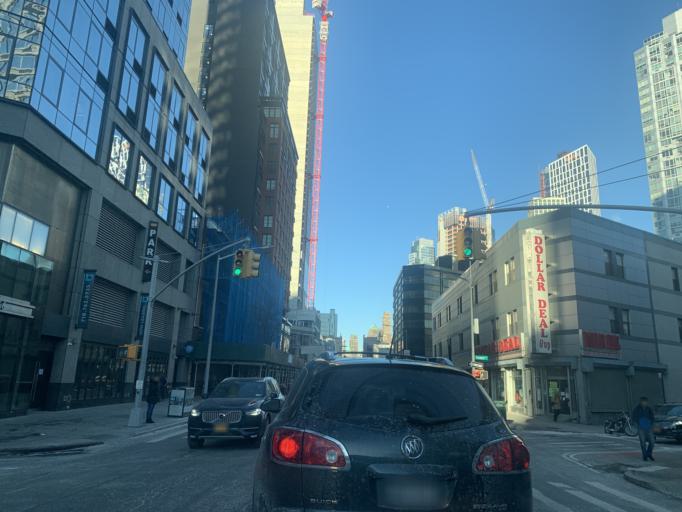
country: US
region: New York
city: New York City
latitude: 40.6883
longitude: -73.9791
